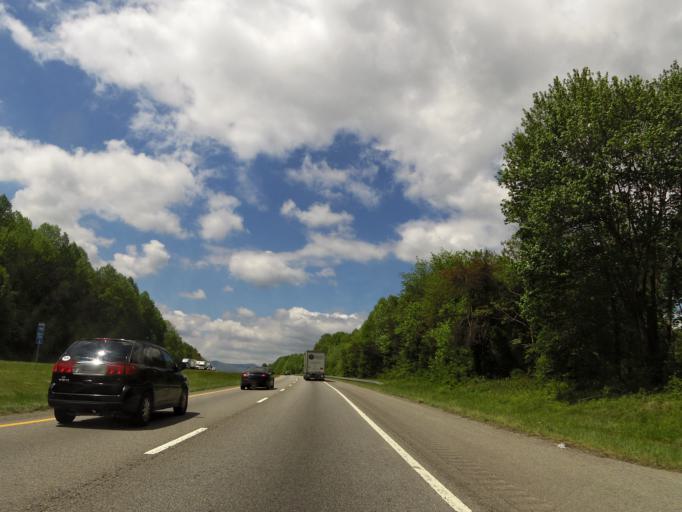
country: US
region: Tennessee
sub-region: Anderson County
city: Norris
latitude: 36.1882
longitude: -84.1001
